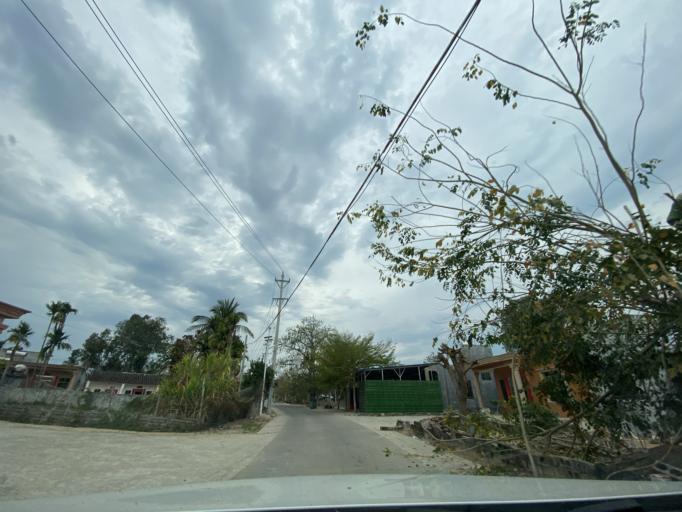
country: CN
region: Hainan
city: Yingzhou
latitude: 18.4172
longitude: 109.8231
